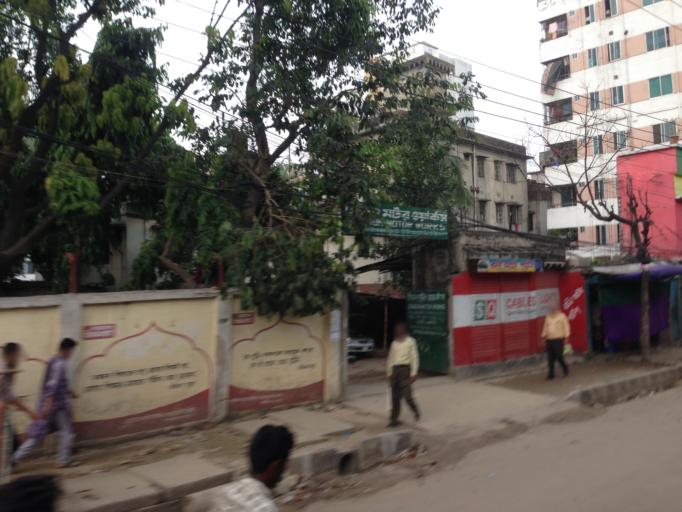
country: BD
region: Dhaka
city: Paltan
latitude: 23.7351
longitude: 90.4287
